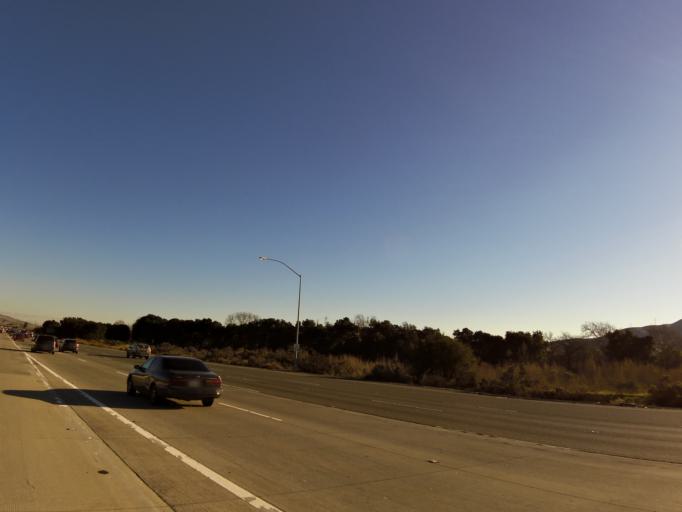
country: US
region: California
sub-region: Santa Clara County
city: Seven Trees
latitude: 37.2375
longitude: -121.7613
